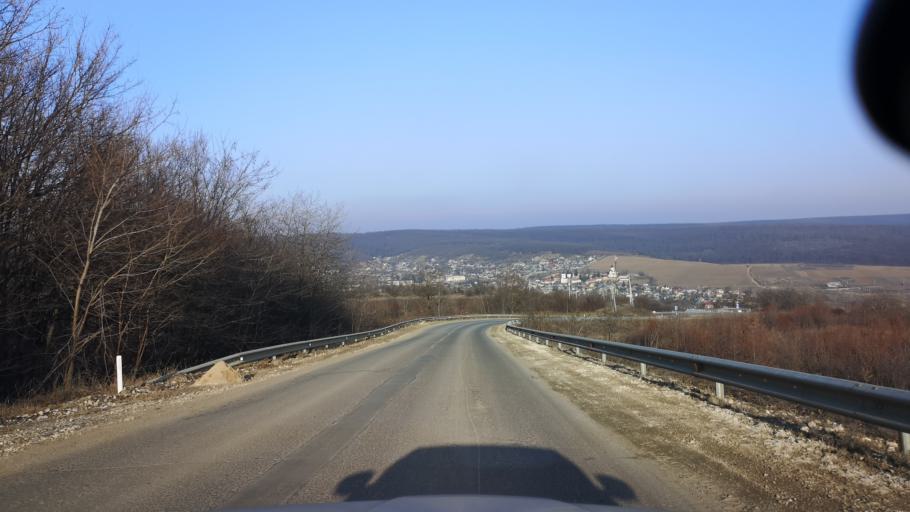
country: MD
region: Stinga Nistrului
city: Bucovat
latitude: 47.1046
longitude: 28.4957
